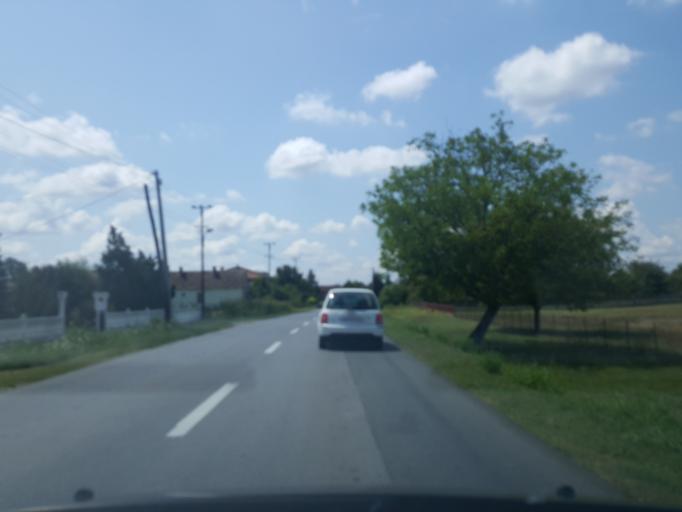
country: RS
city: Salas Nocajski
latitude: 44.9396
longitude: 19.5747
